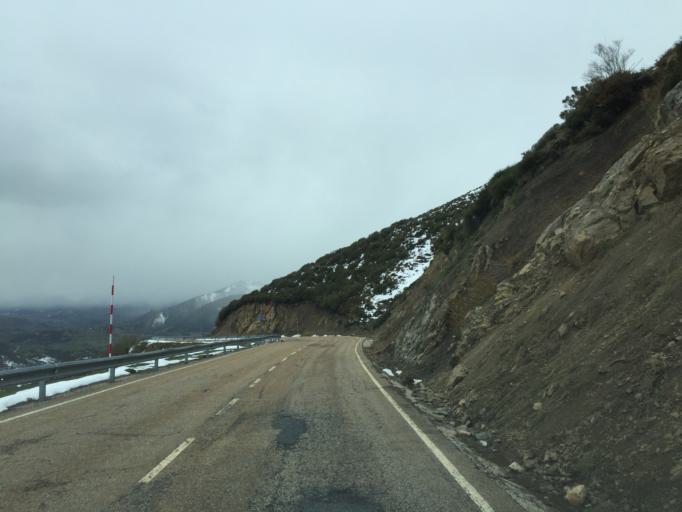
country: ES
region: Castille and Leon
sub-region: Provincia de Leon
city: San Emiliano
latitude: 43.0562
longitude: -6.0066
